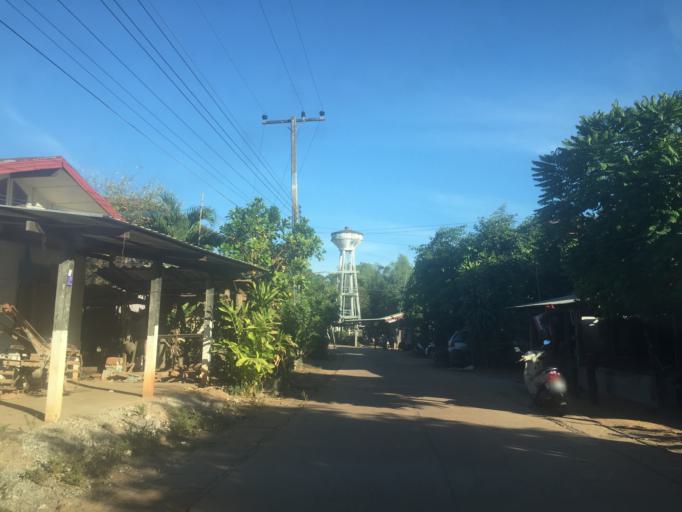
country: TH
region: Changwat Udon Thani
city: Si That
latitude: 16.9685
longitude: 103.2309
